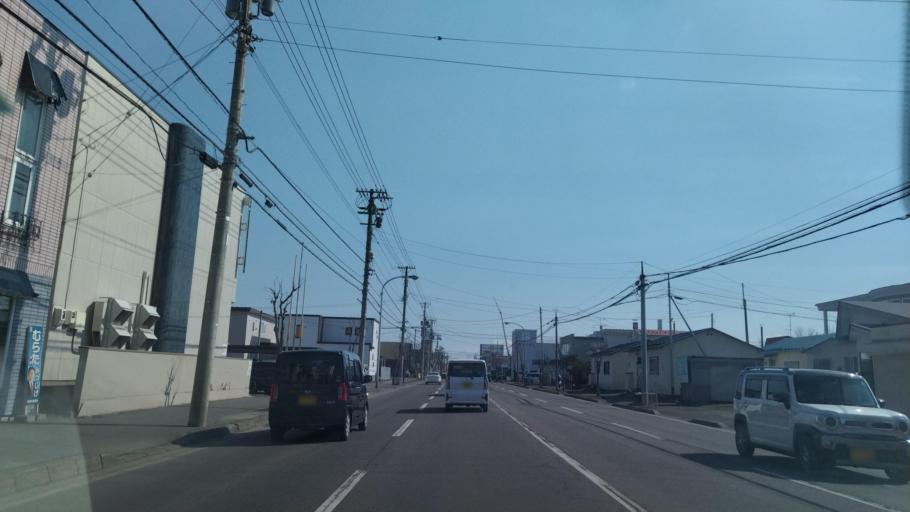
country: JP
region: Hokkaido
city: Obihiro
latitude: 42.8983
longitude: 143.2005
